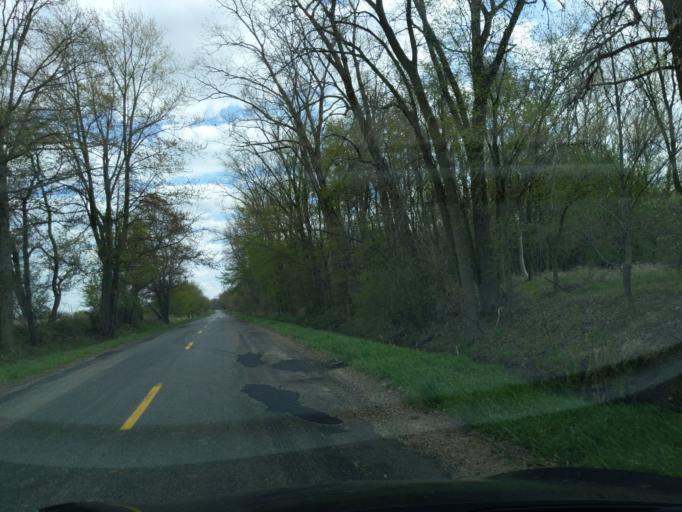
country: US
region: Michigan
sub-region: Eaton County
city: Eaton Rapids
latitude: 42.5196
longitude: -84.5421
